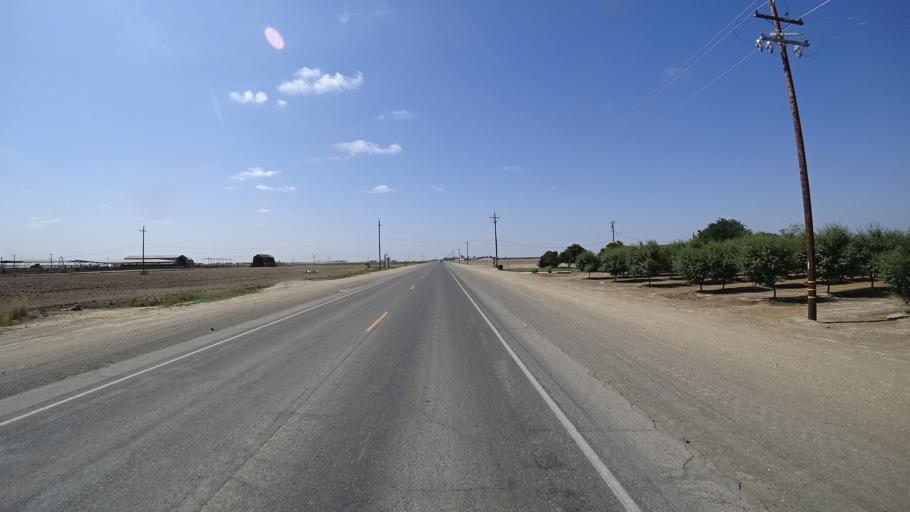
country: US
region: California
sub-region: Kings County
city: Home Garden
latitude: 36.2621
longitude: -119.6369
